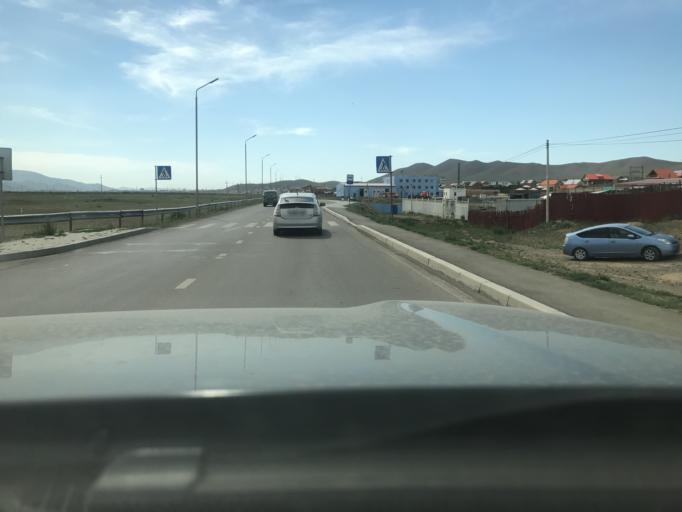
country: MN
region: Ulaanbaatar
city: Ulaanbaatar
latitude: 47.9157
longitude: 107.0935
